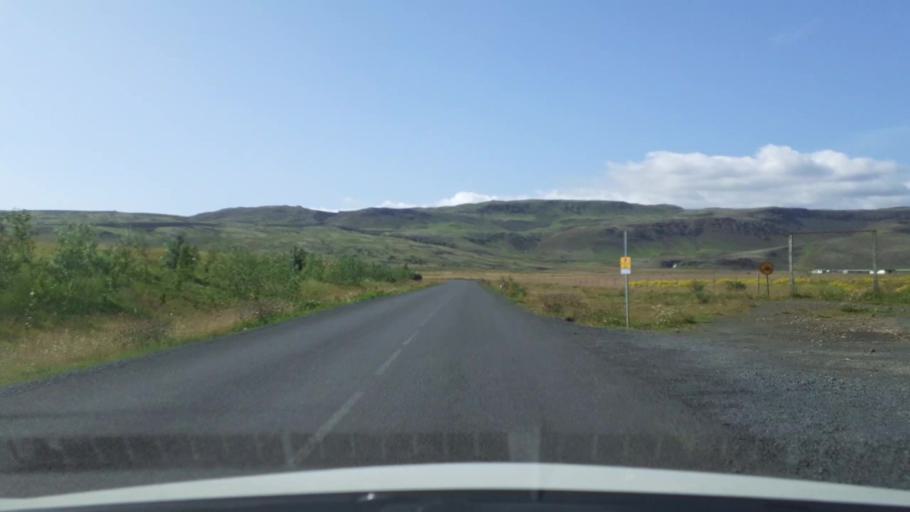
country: IS
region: South
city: Hveragerdi
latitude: 64.0123
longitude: -21.1939
